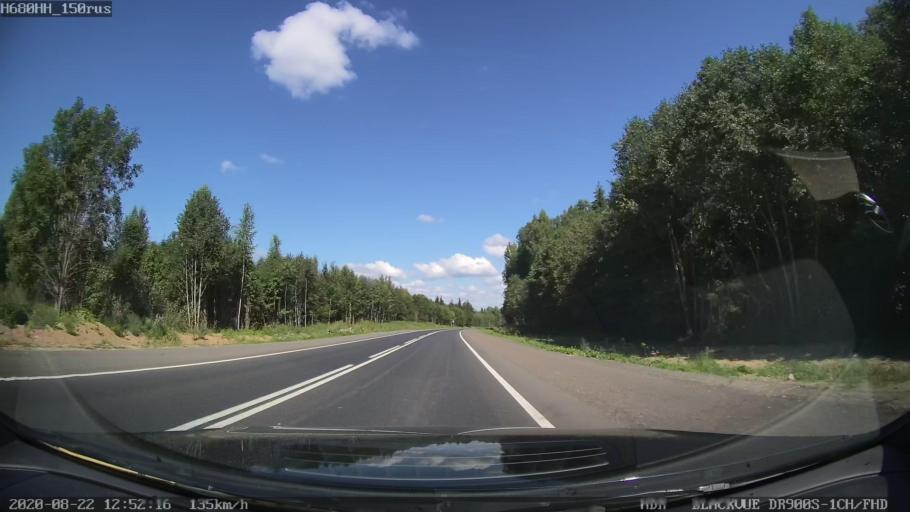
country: RU
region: Tverskaya
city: Rameshki
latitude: 57.4996
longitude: 36.2587
